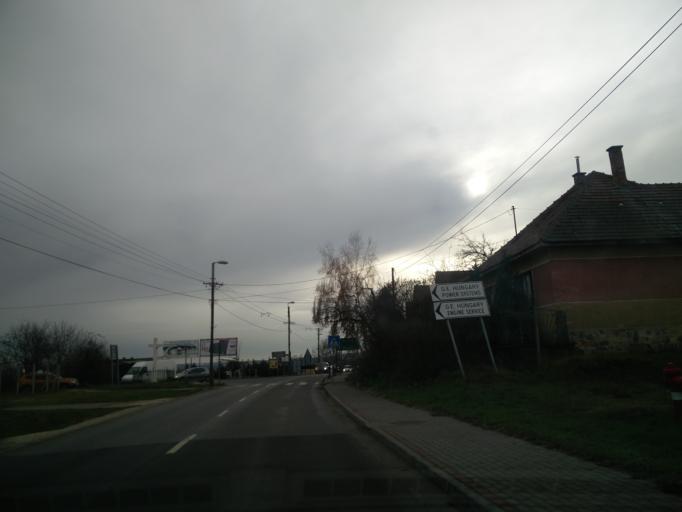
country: HU
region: Pest
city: Mogyorod
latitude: 47.6514
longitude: 19.2365
